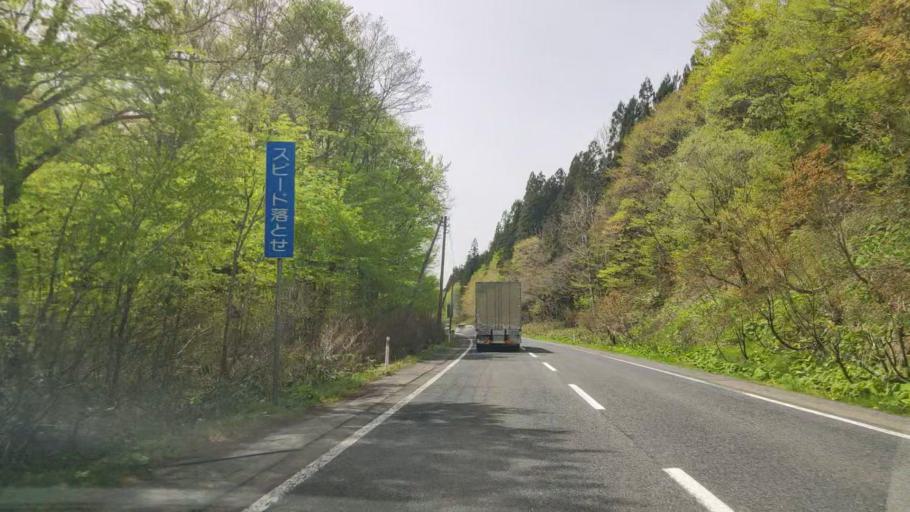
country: JP
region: Aomori
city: Aomori Shi
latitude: 40.7758
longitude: 141.0180
